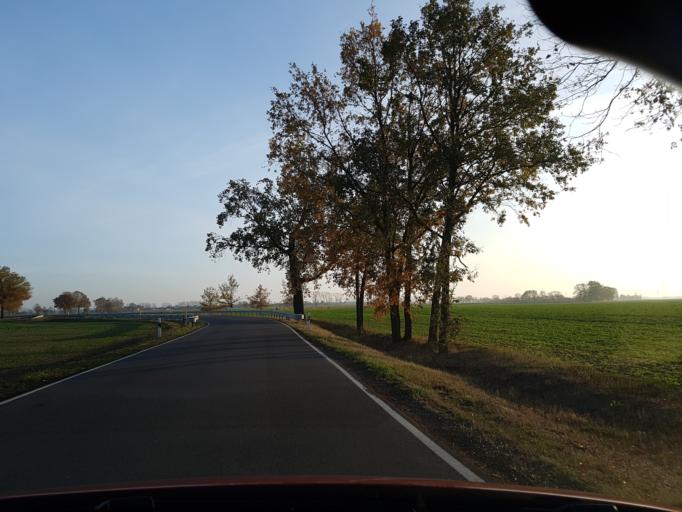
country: DE
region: Brandenburg
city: Bad Liebenwerda
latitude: 51.4746
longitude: 13.4227
